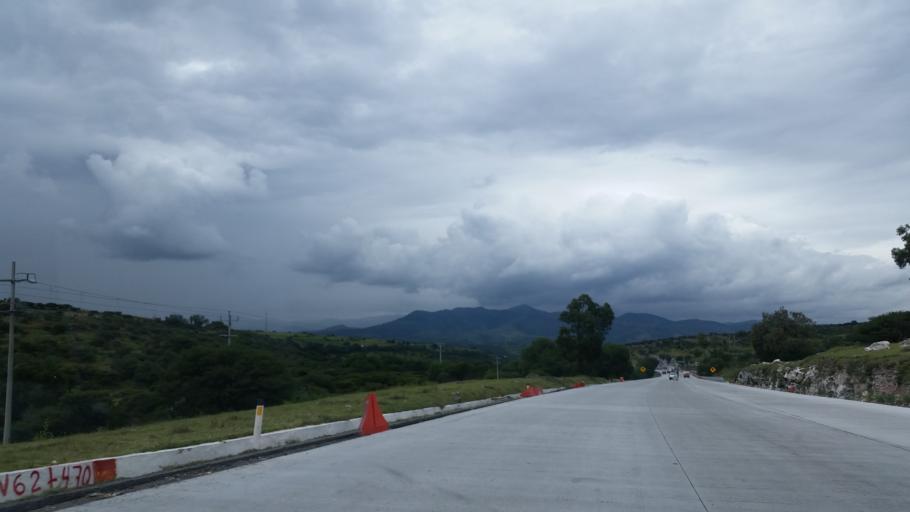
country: MX
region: Hidalgo
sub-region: Tepeji del Rio de Ocampo
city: Cantera de Villagran
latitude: 19.8597
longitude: -99.3030
